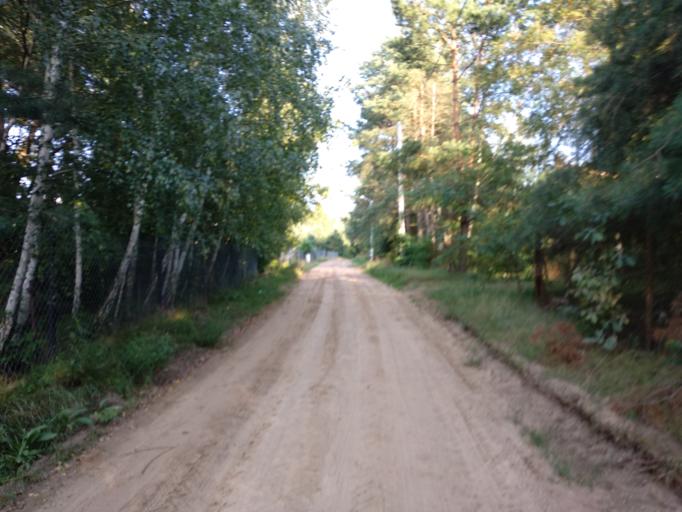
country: PL
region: Masovian Voivodeship
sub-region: Powiat pultuski
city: Obryte
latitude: 52.7569
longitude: 21.1865
